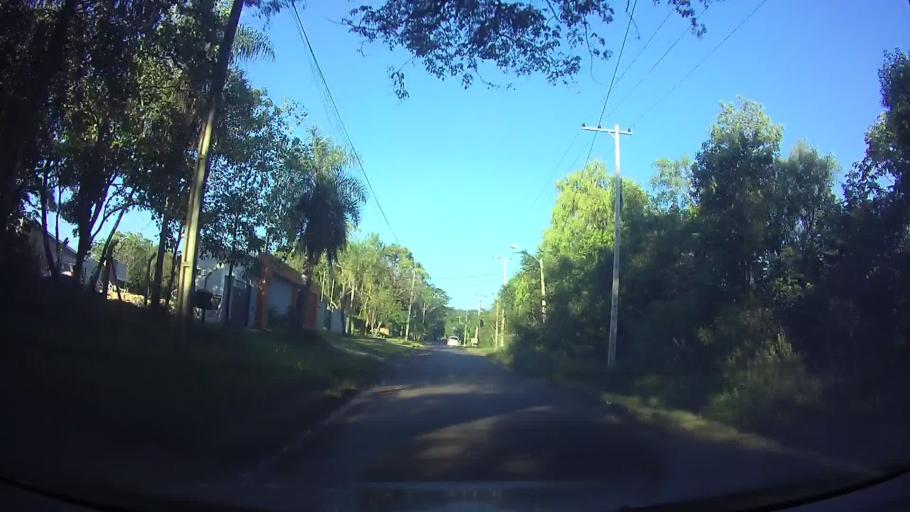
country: PY
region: Cordillera
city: San Bernardino
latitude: -25.3223
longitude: -57.2756
